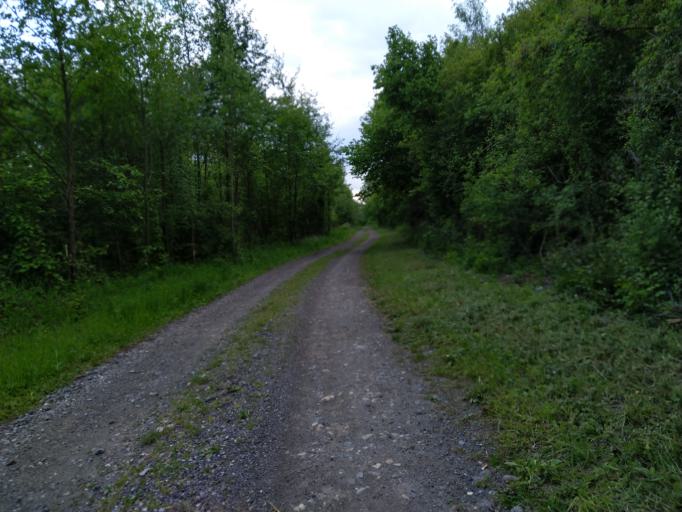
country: FR
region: Picardie
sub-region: Departement de l'Aisne
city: Guise
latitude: 49.9216
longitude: 3.6127
